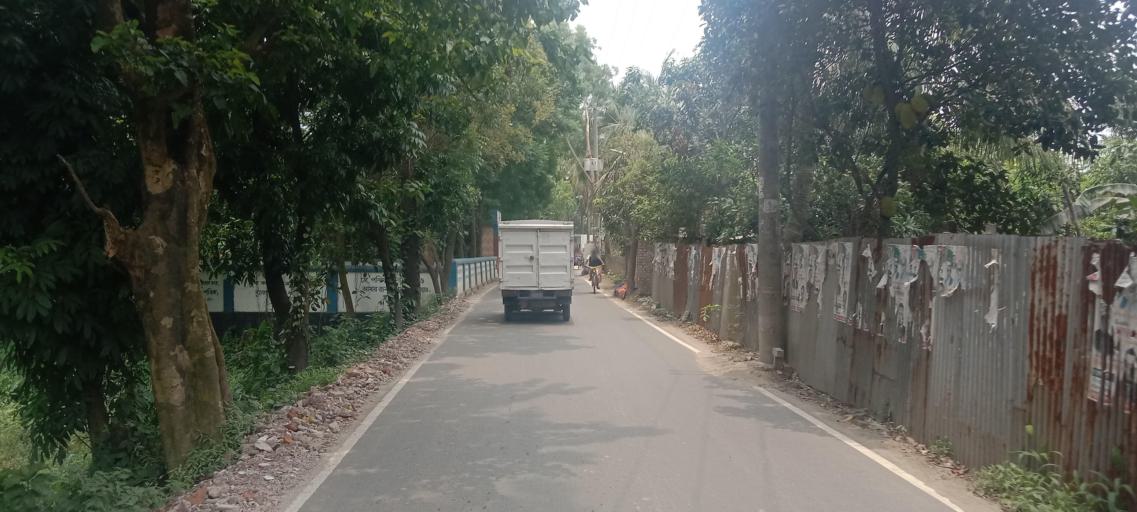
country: BD
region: Dhaka
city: Azimpur
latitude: 23.7192
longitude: 90.3451
